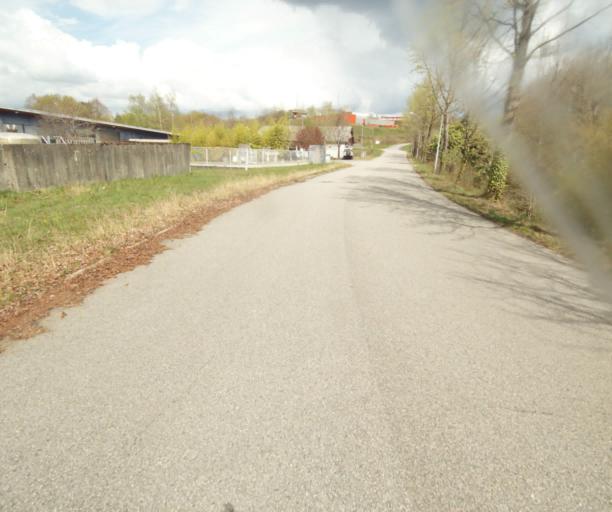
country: FR
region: Limousin
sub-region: Departement de la Correze
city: Tulle
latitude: 45.2781
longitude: 1.7918
